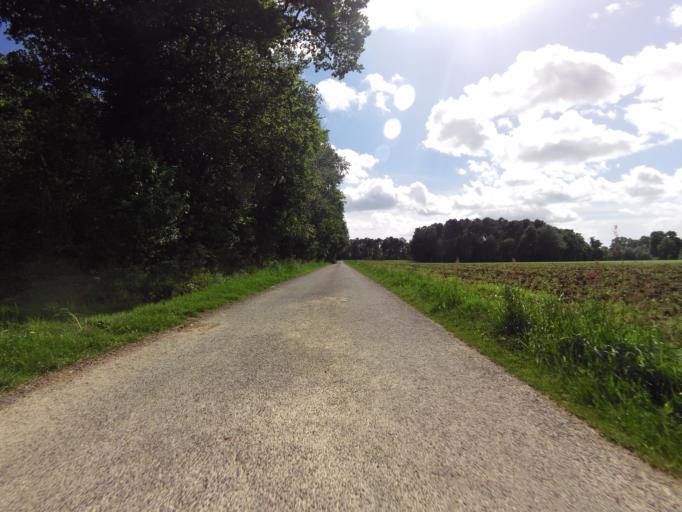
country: FR
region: Brittany
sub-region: Departement du Morbihan
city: Malansac
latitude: 47.7233
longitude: -2.3140
